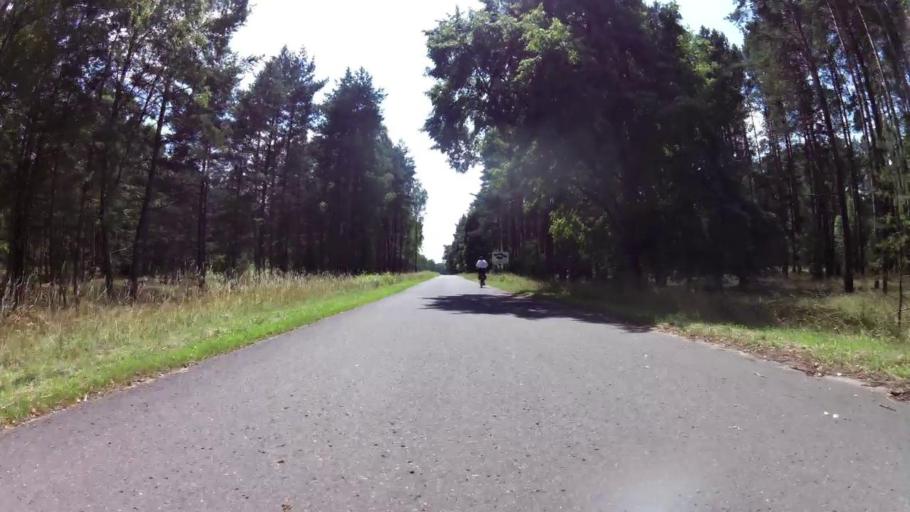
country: PL
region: West Pomeranian Voivodeship
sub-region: Powiat drawski
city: Drawsko Pomorskie
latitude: 53.3860
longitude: 15.7288
